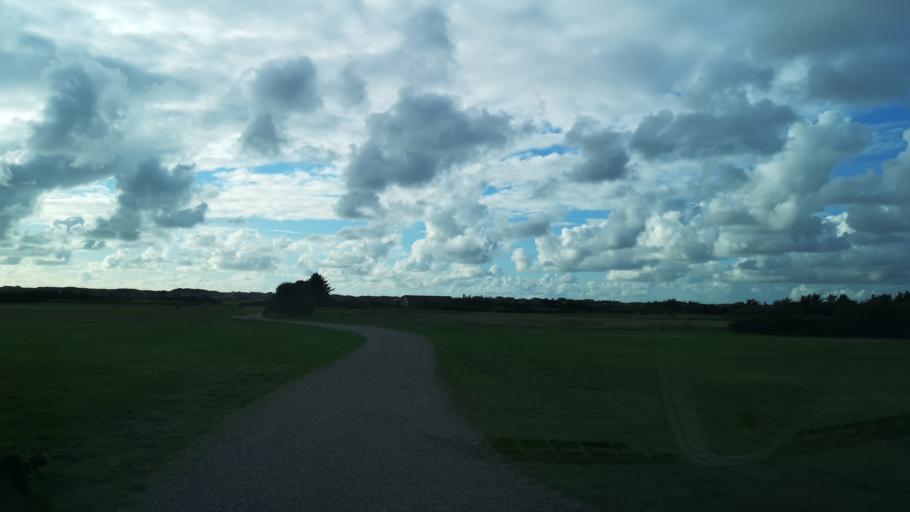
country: DK
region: Central Jutland
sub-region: Ringkobing-Skjern Kommune
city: Ringkobing
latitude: 56.1289
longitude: 8.1305
